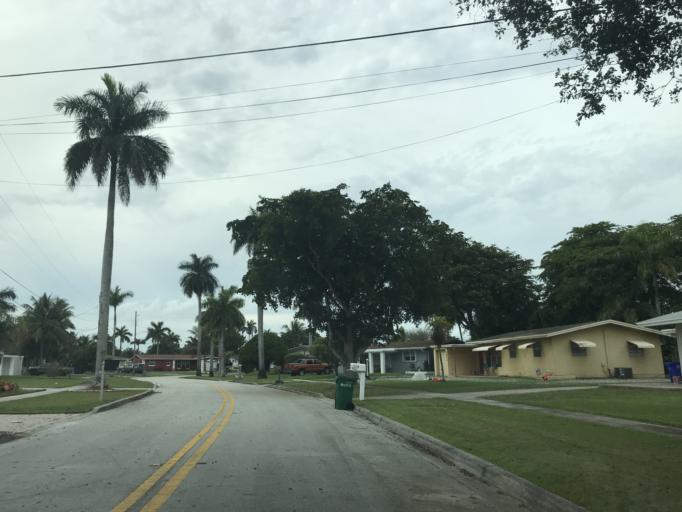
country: US
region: Florida
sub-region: Broward County
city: Margate
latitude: 26.2481
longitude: -80.2051
